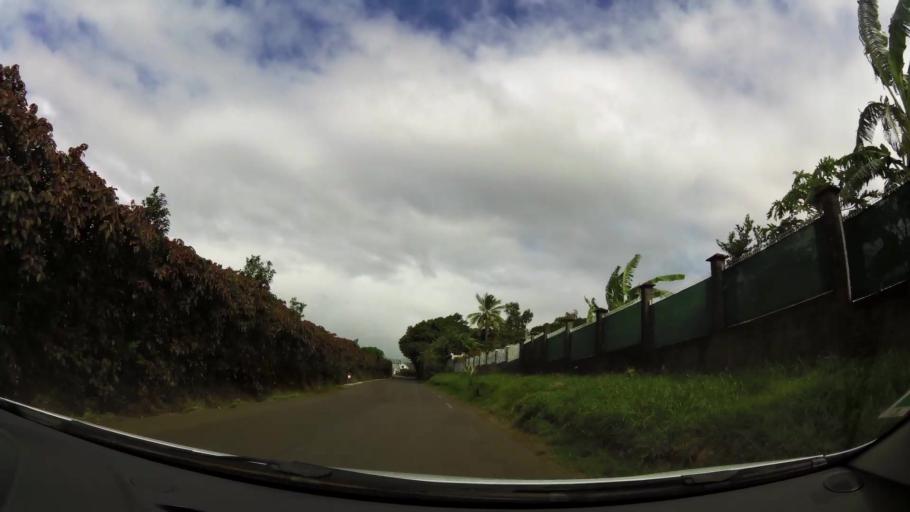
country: RE
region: Reunion
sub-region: Reunion
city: Sainte-Marie
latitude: -20.9012
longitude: 55.5697
